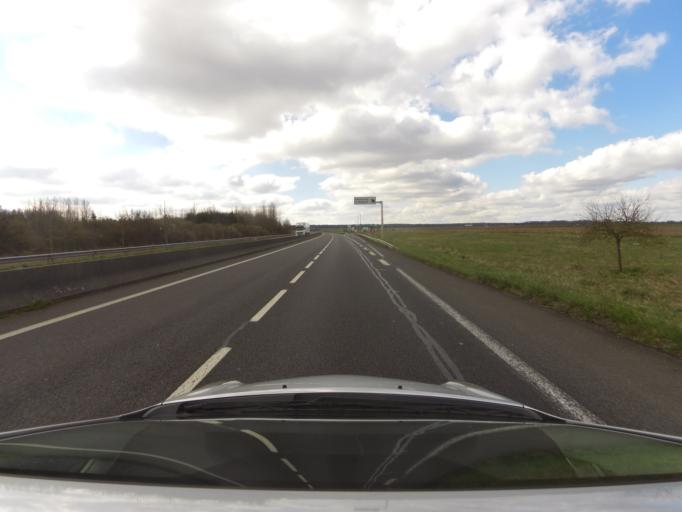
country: FR
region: Picardie
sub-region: Departement de la Somme
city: Bouttencourt
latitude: 49.9663
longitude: 1.6610
